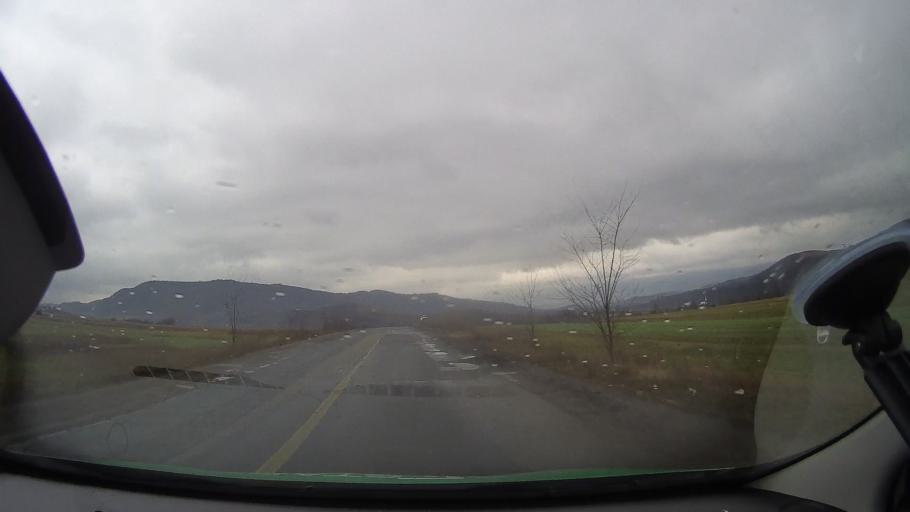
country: RO
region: Arad
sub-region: Comuna Halmagiu
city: Halmagiu
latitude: 46.2330
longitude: 22.5590
